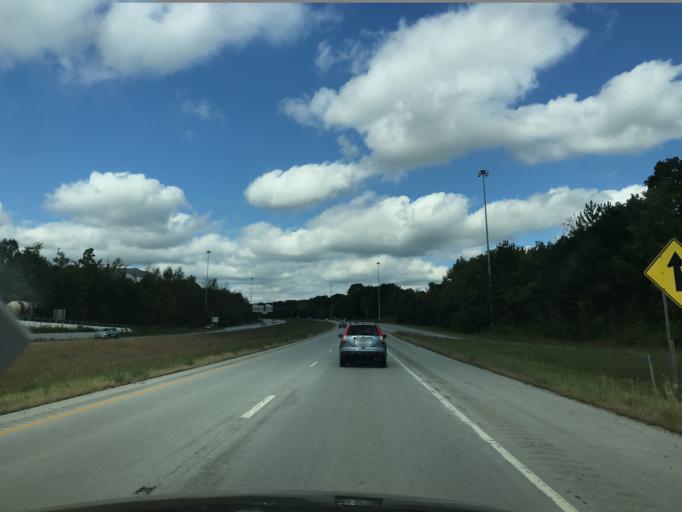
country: US
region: Ohio
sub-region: Summit County
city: Twinsburg
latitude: 41.3122
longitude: -81.4516
